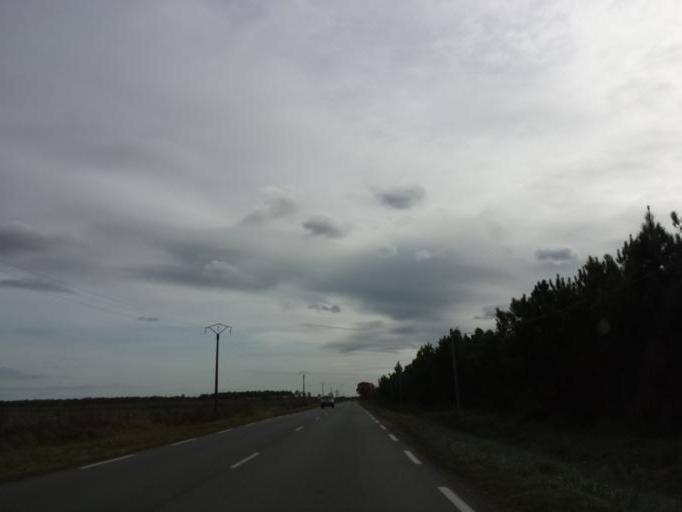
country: FR
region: Aquitaine
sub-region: Departement de la Gironde
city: Marcheprime
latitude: 44.7697
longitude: -0.9259
